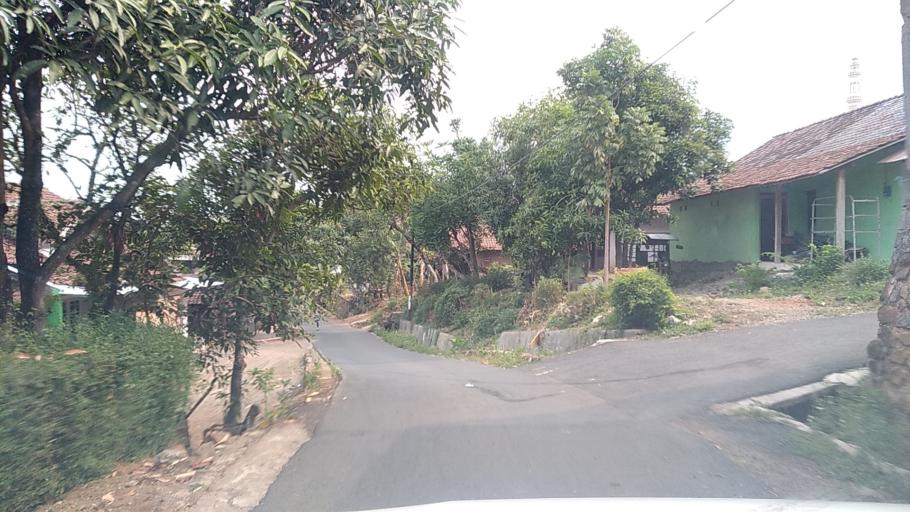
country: ID
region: Central Java
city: Semarang
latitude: -7.0193
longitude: 110.3395
